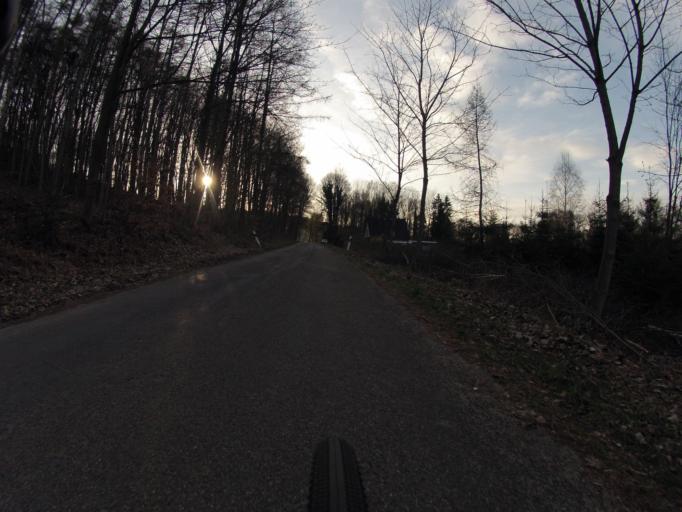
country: DE
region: North Rhine-Westphalia
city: Ibbenburen
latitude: 52.2406
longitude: 7.7484
